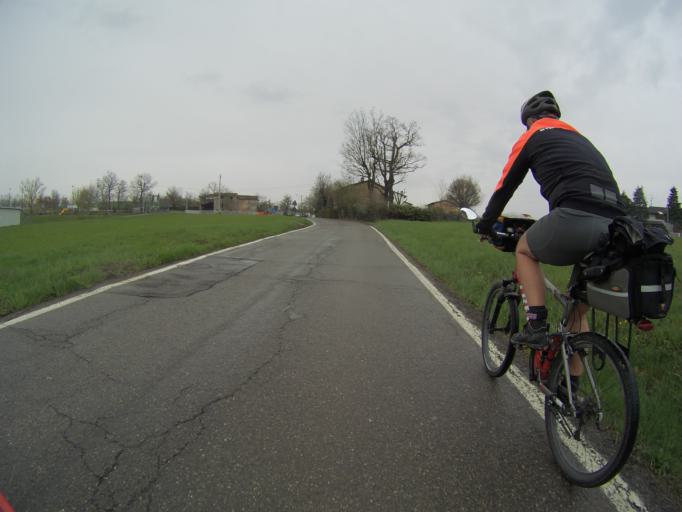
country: IT
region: Emilia-Romagna
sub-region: Provincia di Reggio Emilia
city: Ciano d'Enza
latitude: 44.5411
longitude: 10.4161
